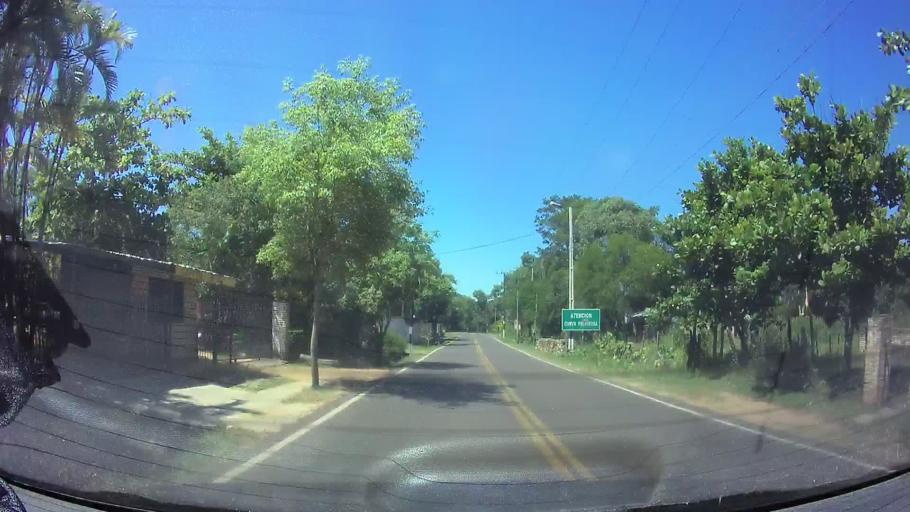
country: PY
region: Central
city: Aregua
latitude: -25.2684
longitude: -57.4128
